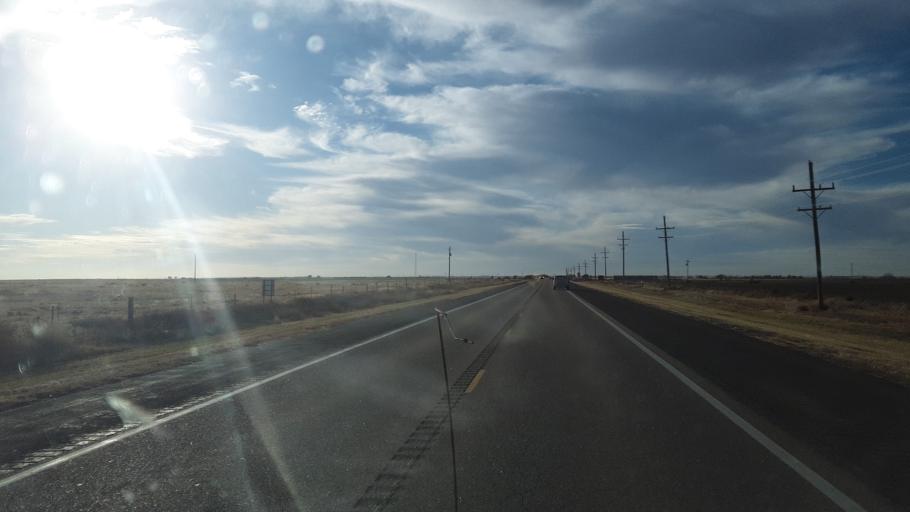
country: US
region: Kansas
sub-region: Kearny County
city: Lakin
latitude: 37.9736
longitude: -101.1721
